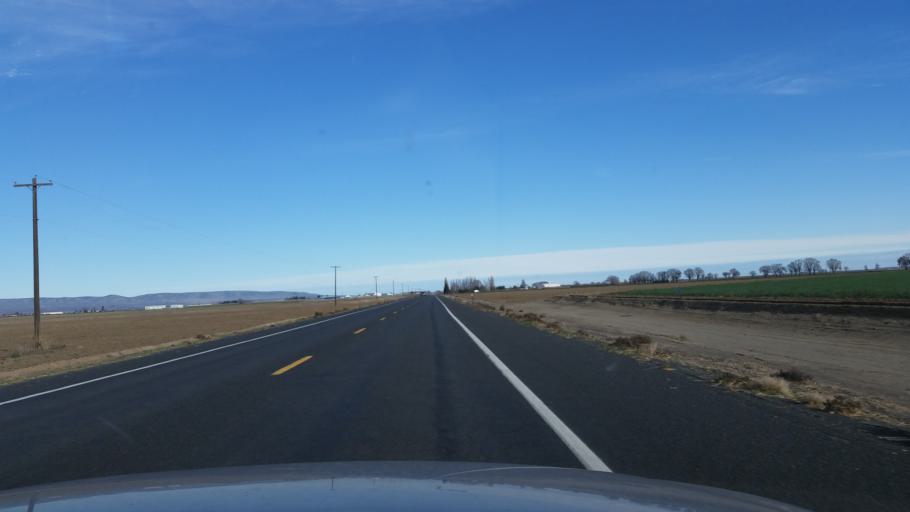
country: US
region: Washington
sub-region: Grant County
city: Quincy
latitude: 47.1341
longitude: -119.7827
